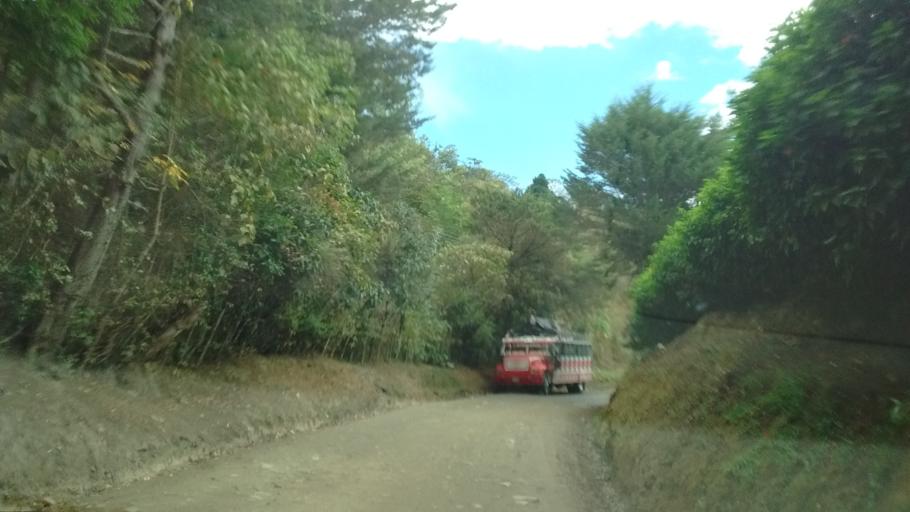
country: CO
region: Cauca
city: Almaguer
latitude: 1.8470
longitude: -76.9238
